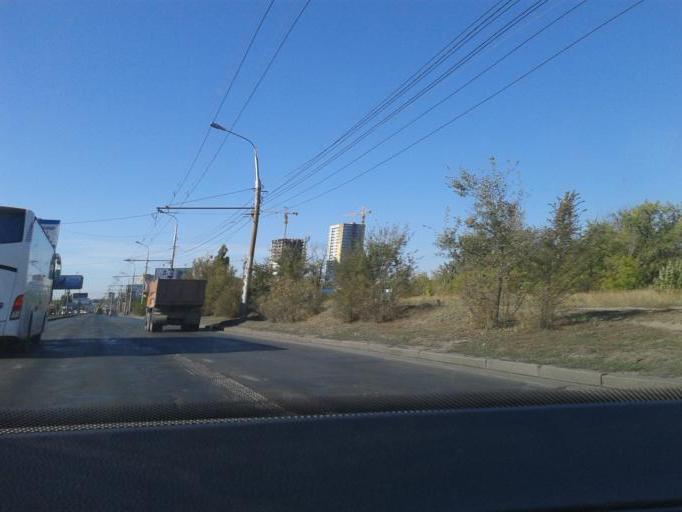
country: RU
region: Volgograd
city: Volgograd
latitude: 48.6309
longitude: 44.4281
